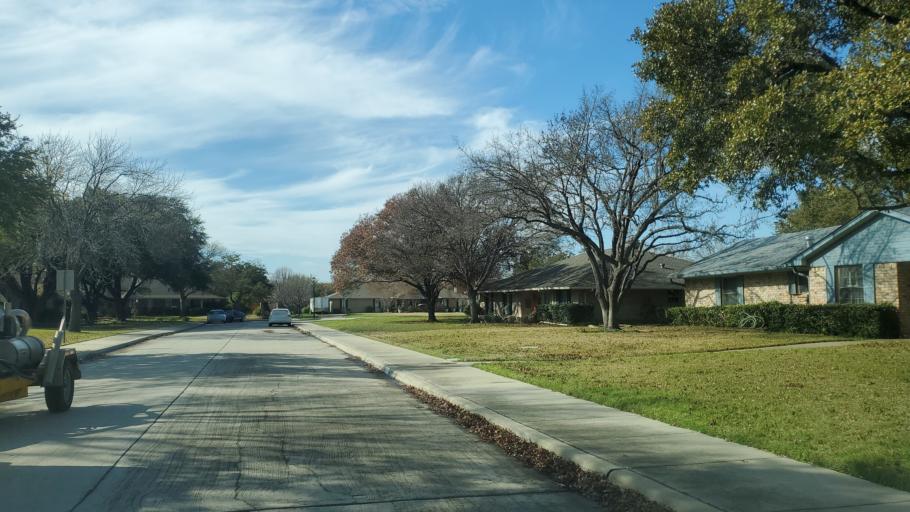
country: US
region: Texas
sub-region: Dallas County
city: Carrollton
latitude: 32.9828
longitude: -96.8912
